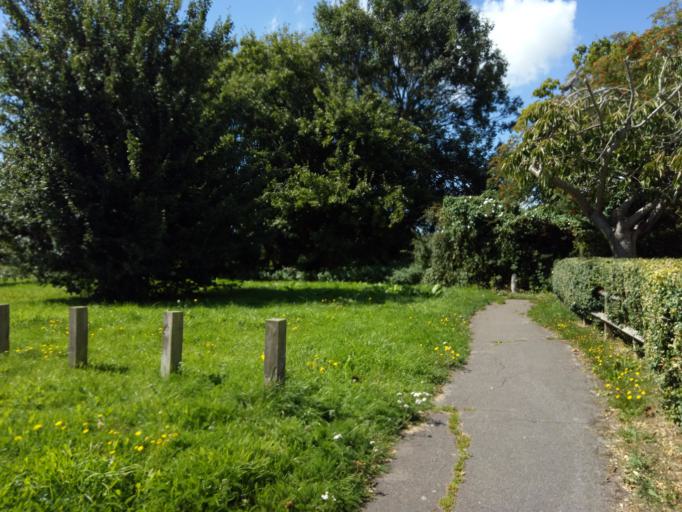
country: GB
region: England
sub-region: West Sussex
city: Barnham
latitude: 50.7928
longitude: -0.6373
